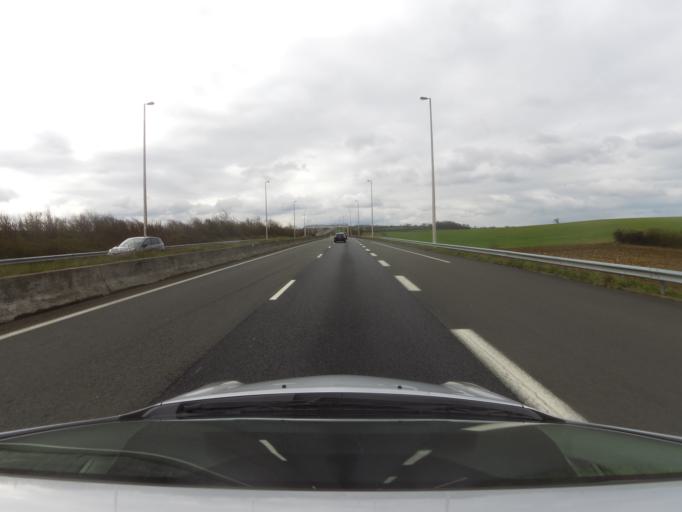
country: FR
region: Nord-Pas-de-Calais
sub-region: Departement du Pas-de-Calais
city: Marquise
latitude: 50.8032
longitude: 1.6913
